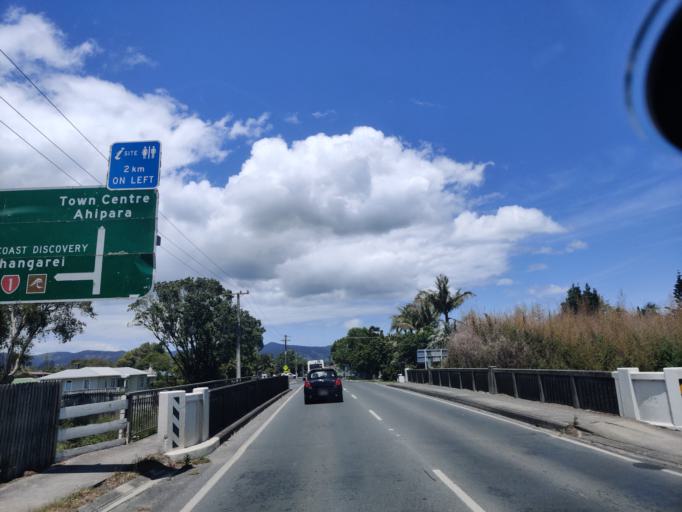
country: NZ
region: Northland
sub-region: Far North District
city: Kaitaia
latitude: -35.1020
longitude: 173.2594
